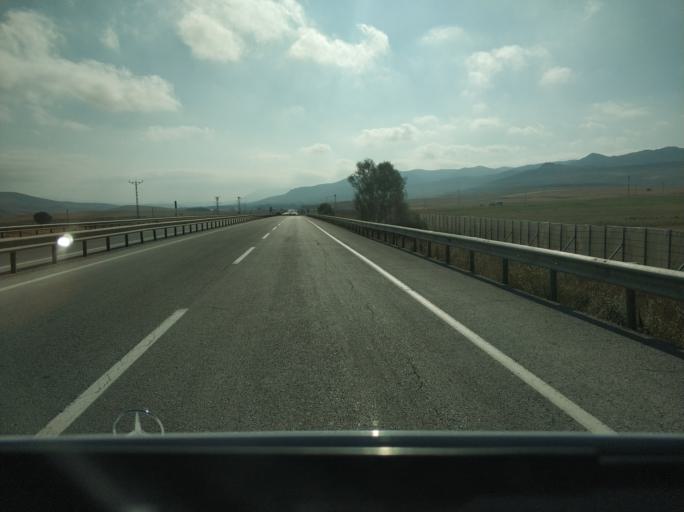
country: TR
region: Sivas
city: Yildizeli
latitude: 39.8348
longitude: 36.4234
